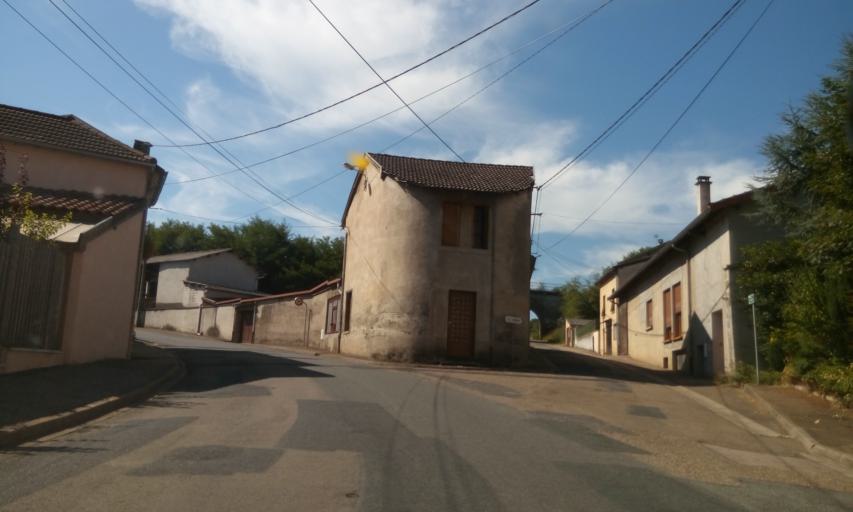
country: FR
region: Rhone-Alpes
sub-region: Departement du Rhone
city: Amplepuis
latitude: 45.9733
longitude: 4.3246
